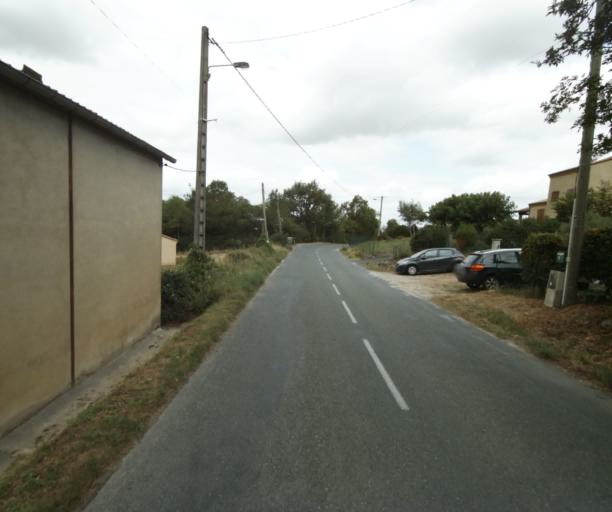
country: FR
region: Midi-Pyrenees
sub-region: Departement du Tarn
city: Soreze
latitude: 43.4502
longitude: 2.0732
